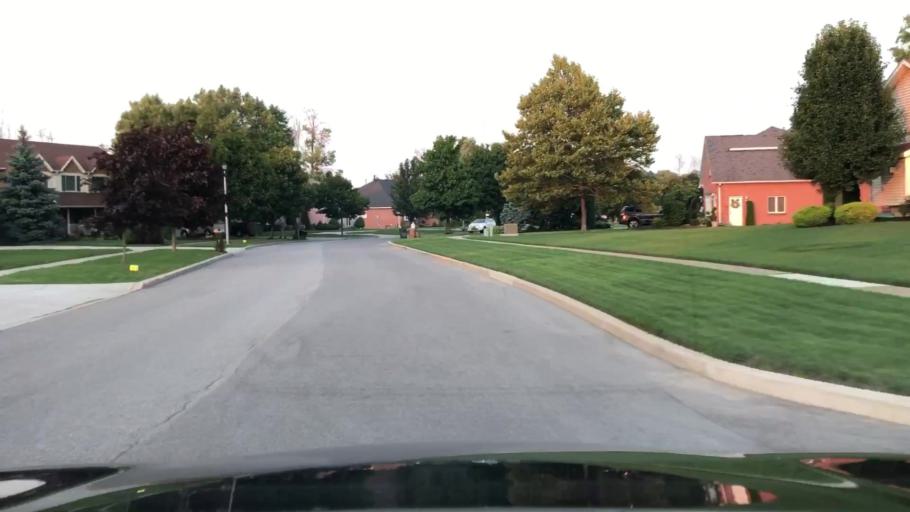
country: US
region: New York
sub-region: Erie County
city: Depew
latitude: 42.8670
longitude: -78.6897
